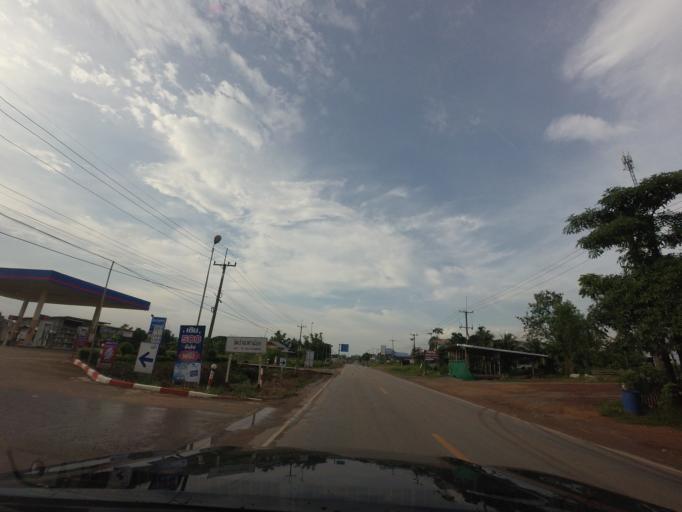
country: TH
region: Nong Khai
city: Pho Tak
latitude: 17.7728
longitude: 102.3958
